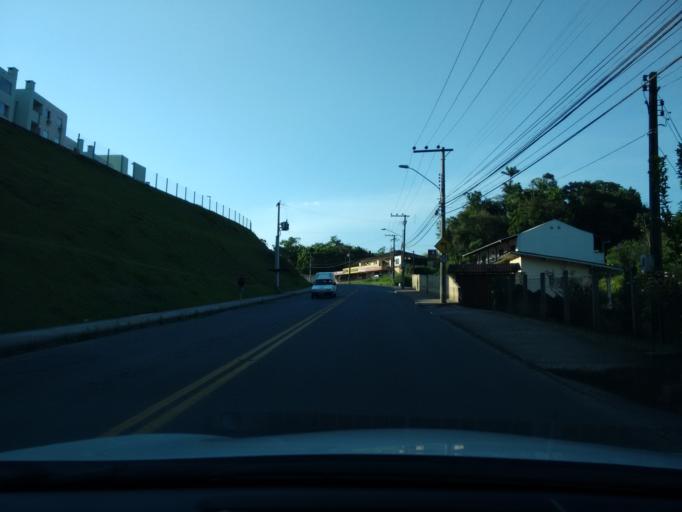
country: BR
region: Santa Catarina
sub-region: Blumenau
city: Blumenau
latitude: -26.8582
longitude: -49.1057
